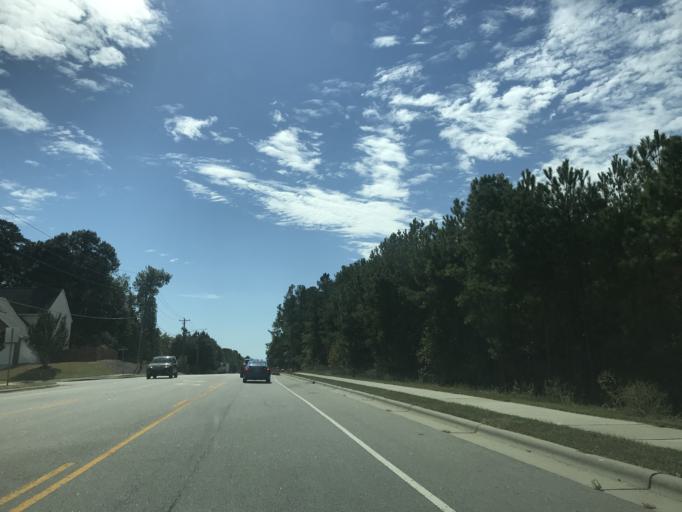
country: US
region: North Carolina
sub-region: Wake County
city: Knightdale
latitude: 35.8614
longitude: -78.5667
